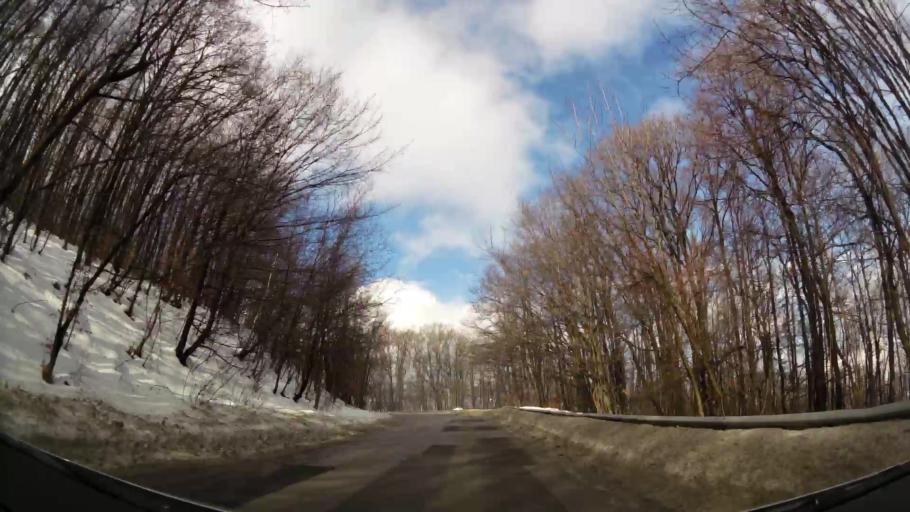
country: BG
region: Sofiya
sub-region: Obshtina Bozhurishte
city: Bozhurishte
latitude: 42.6417
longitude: 23.2186
